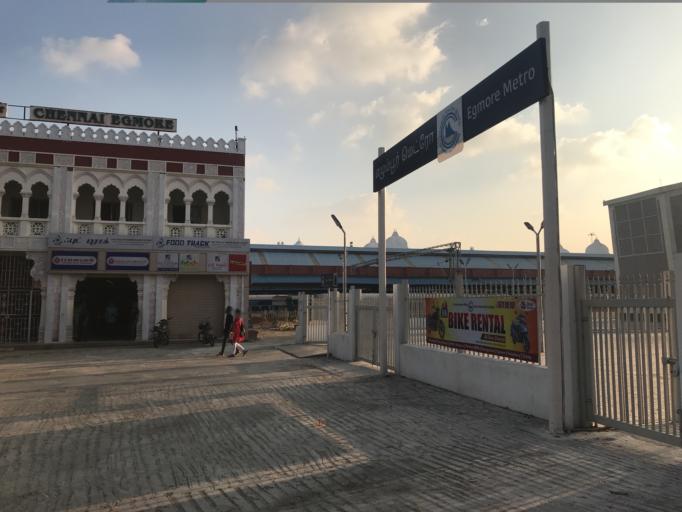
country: IN
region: Tamil Nadu
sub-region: Chennai
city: Chennai
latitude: 13.0793
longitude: 80.2619
